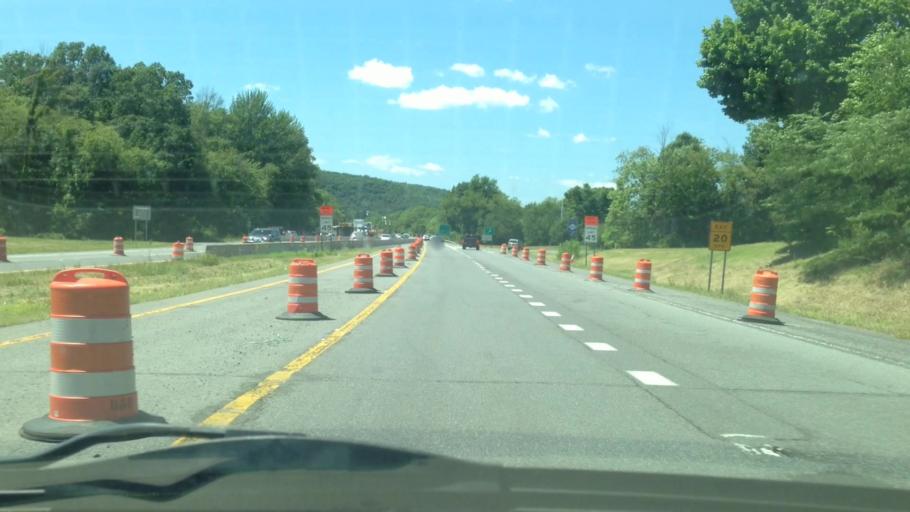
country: US
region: New York
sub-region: Ulster County
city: Lake Katrine
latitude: 41.9758
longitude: -73.9996
